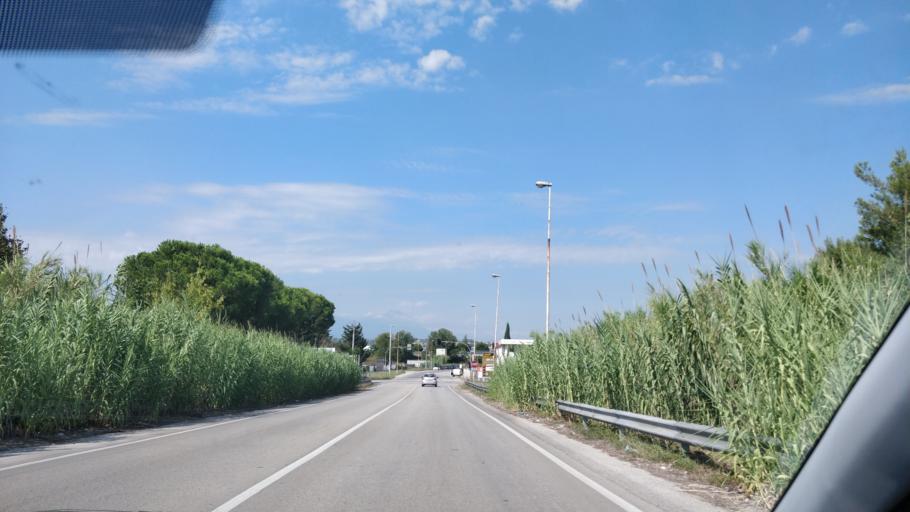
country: IT
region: Abruzzo
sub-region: Provincia di Pescara
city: Santa Teresa
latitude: 42.4081
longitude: 14.1665
